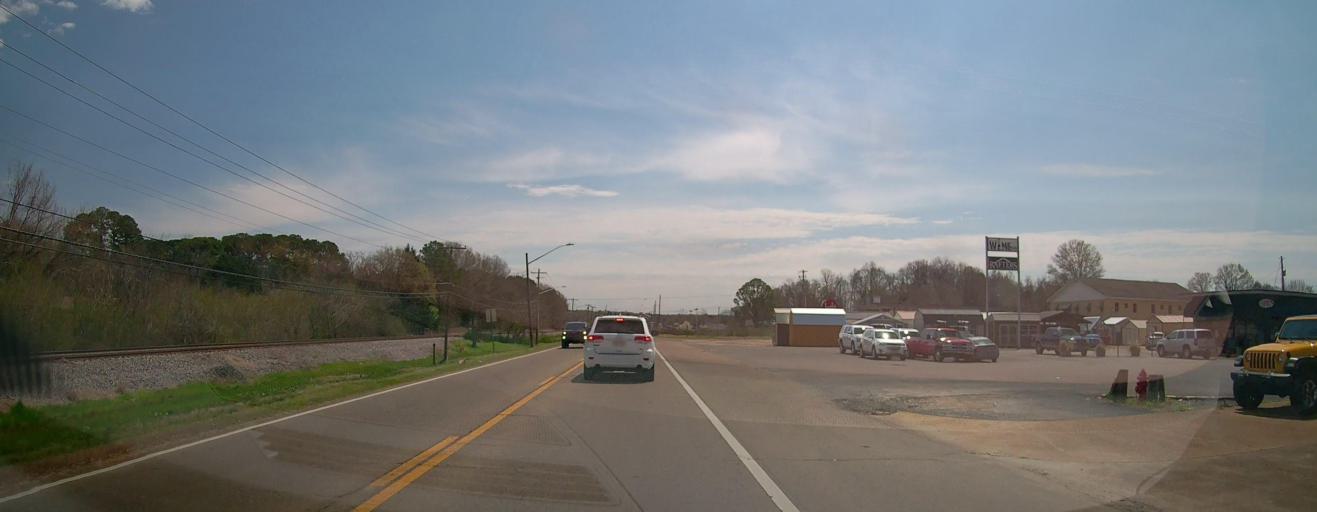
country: US
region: Mississippi
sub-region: Union County
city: New Albany
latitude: 34.5017
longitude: -89.0264
